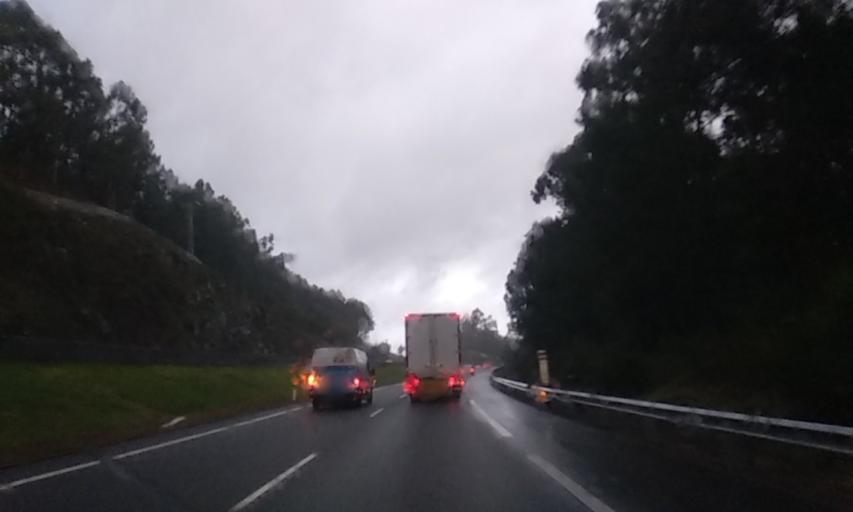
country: ES
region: Galicia
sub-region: Provincia de Pontevedra
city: Marin
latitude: 42.3405
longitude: -8.6485
